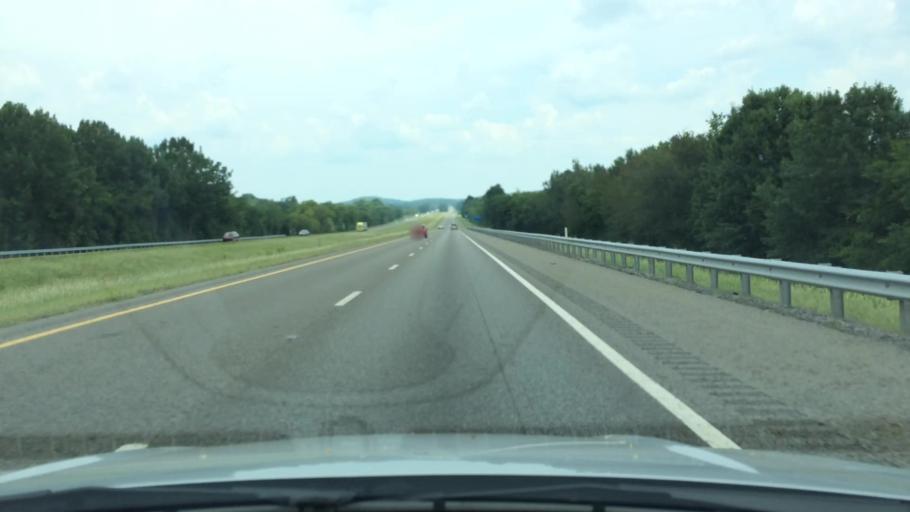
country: US
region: Tennessee
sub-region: Marshall County
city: Cornersville
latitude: 35.4253
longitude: -86.8785
